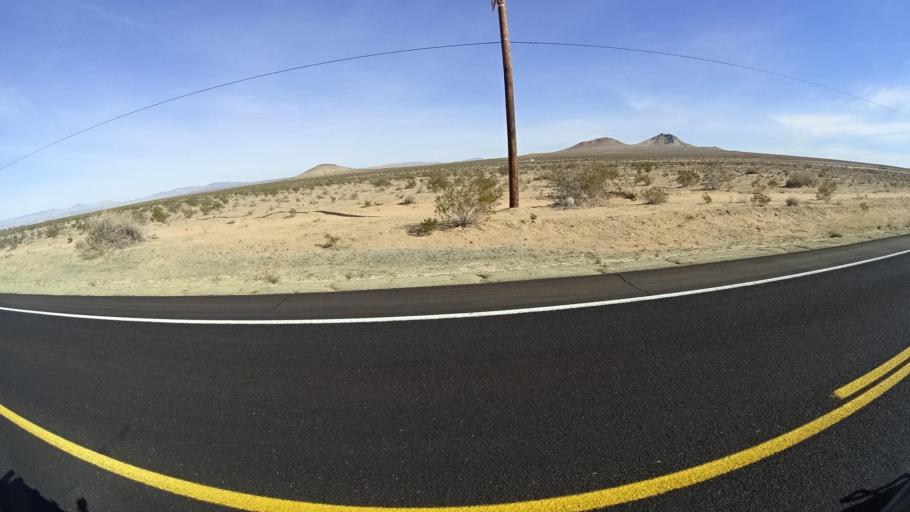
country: US
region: California
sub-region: Kern County
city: California City
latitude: 35.1033
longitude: -117.9193
